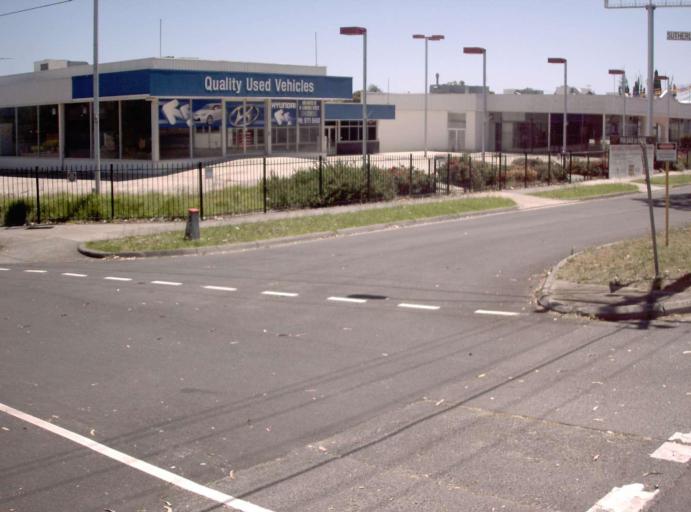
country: AU
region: Victoria
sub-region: Greater Dandenong
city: Dandenong
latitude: -37.9745
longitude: 145.2026
